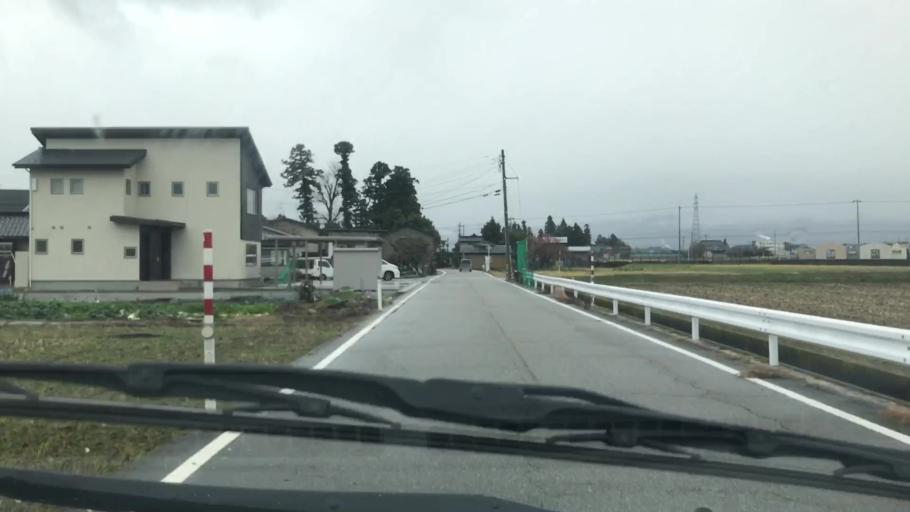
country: JP
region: Toyama
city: Toyama-shi
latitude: 36.6743
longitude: 137.2873
